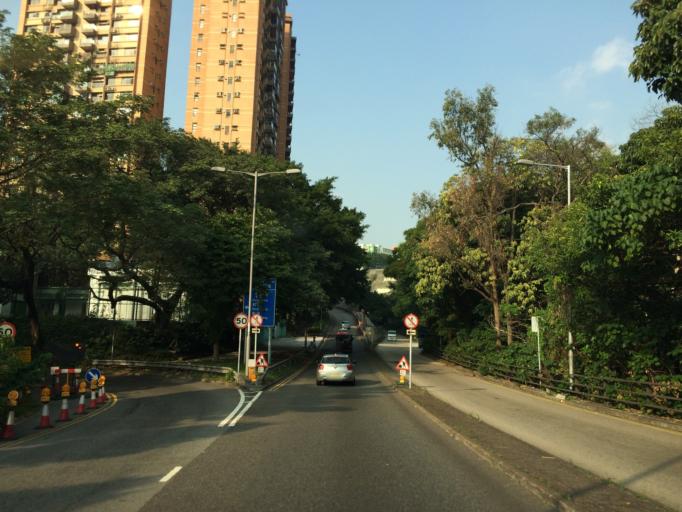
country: HK
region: Kowloon City
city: Kowloon
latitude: 22.3062
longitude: 114.1786
